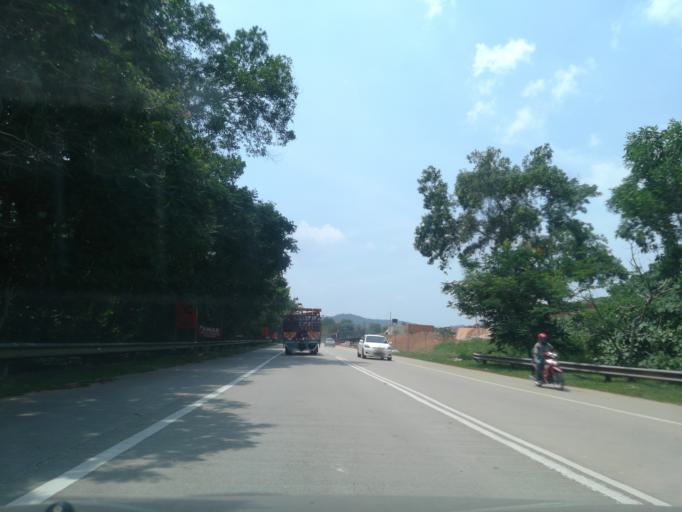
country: MY
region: Kedah
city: Kulim
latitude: 5.4270
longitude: 100.5635
